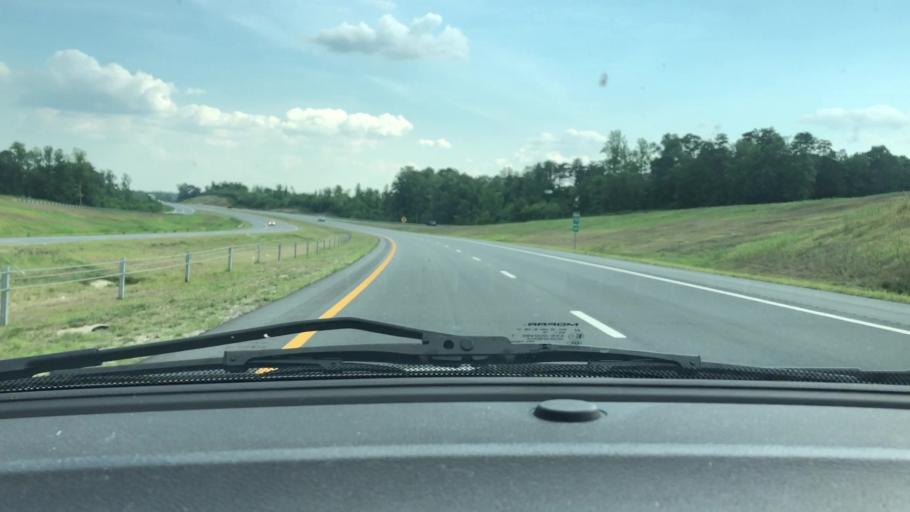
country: US
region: North Carolina
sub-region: Guilford County
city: Summerfield
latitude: 36.2025
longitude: -79.9280
